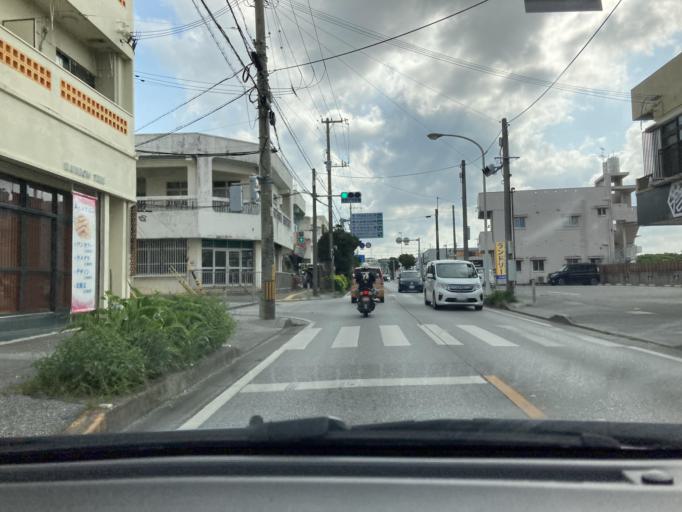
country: JP
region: Okinawa
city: Tomigusuku
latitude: 26.1708
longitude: 127.7412
